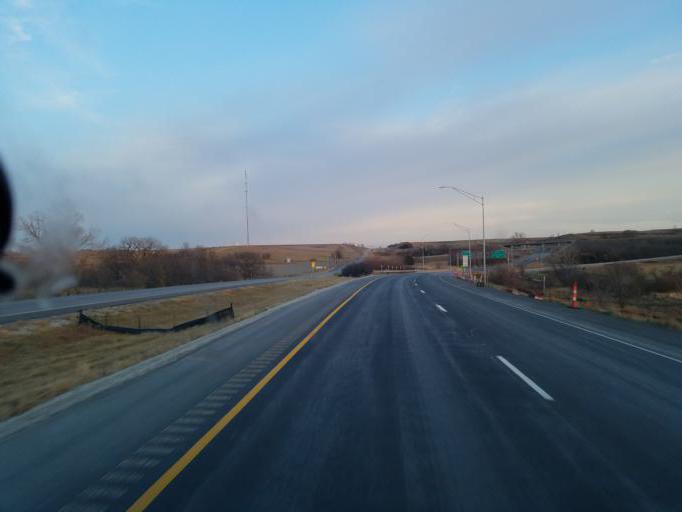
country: US
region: Iowa
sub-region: Harrison County
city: Logan
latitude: 41.4988
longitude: -95.5931
